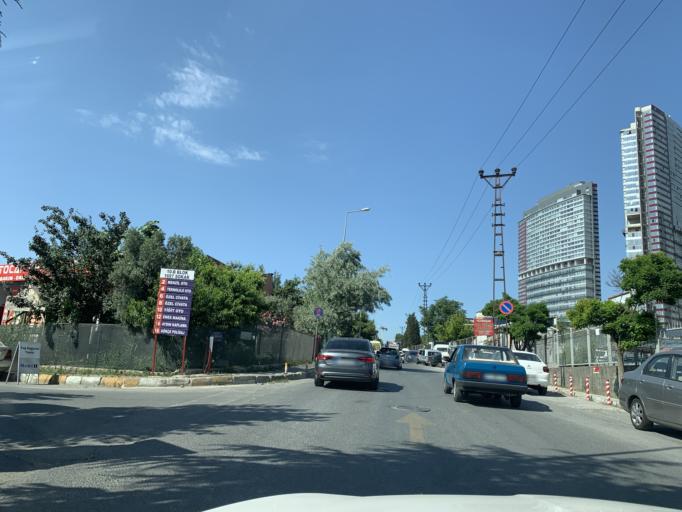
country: TR
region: Istanbul
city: Esenyurt
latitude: 41.0601
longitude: 28.6620
